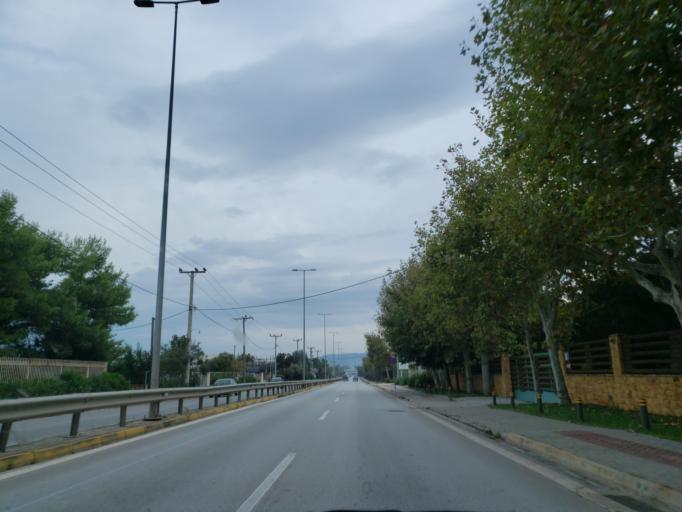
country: GR
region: Attica
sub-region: Nomarchia Anatolikis Attikis
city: Aghios Panteleimon
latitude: 38.1117
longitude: 23.9697
